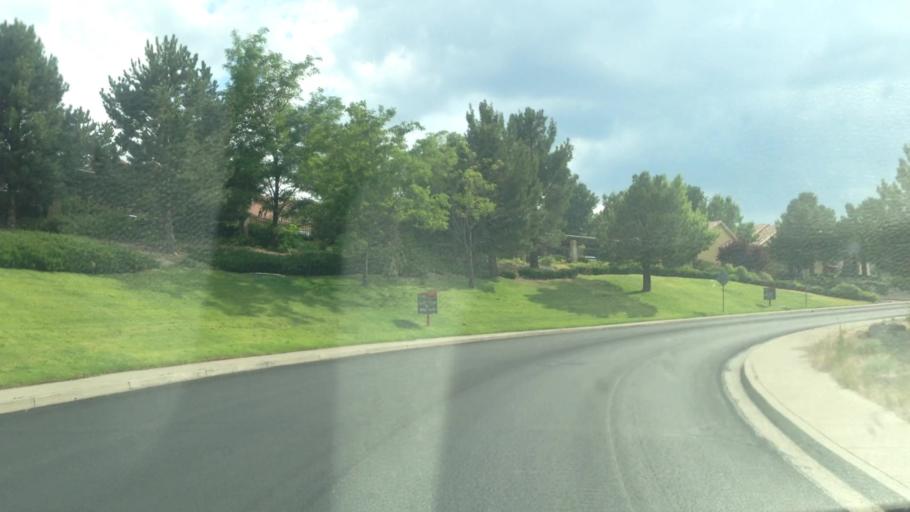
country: US
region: Nevada
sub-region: Washoe County
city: Reno
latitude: 39.5265
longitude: -119.8646
